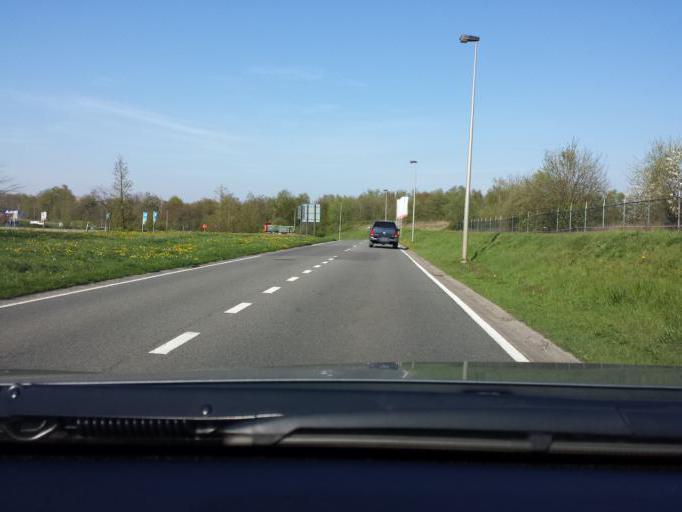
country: BE
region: Flanders
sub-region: Provincie Limburg
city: Maasmechelen
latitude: 50.9852
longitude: 5.7032
